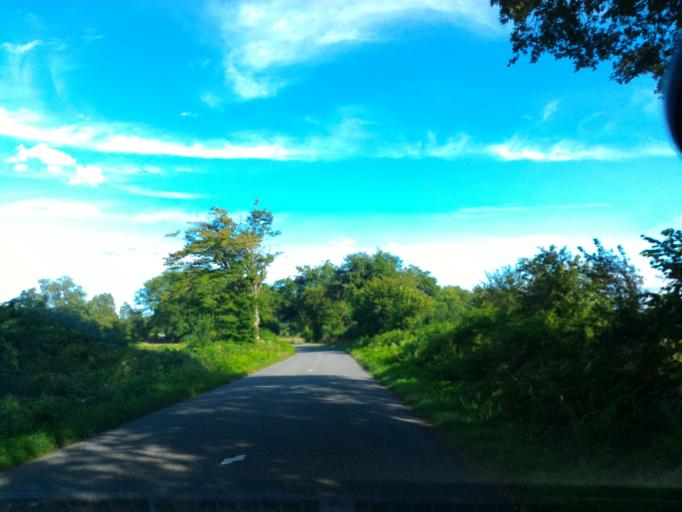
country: FR
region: Poitou-Charentes
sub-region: Departement de la Charente
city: Brigueuil
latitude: 45.9988
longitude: 0.8565
